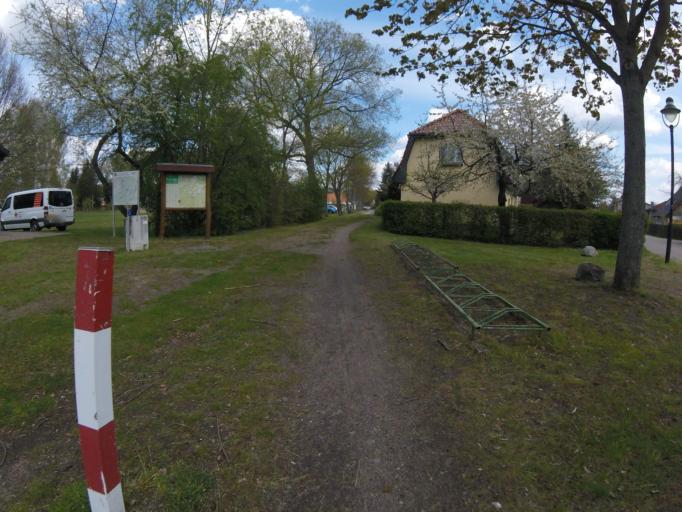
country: DE
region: Brandenburg
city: Munchehofe
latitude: 52.2232
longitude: 13.7674
